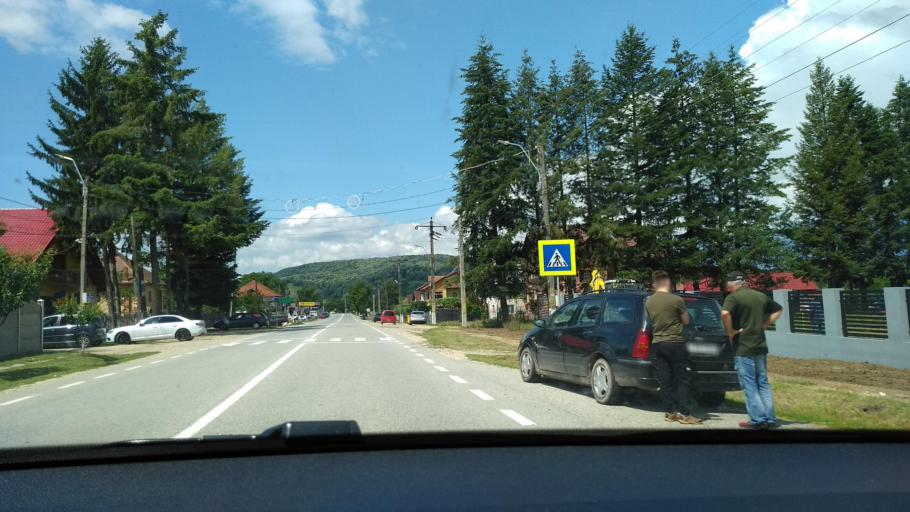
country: RO
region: Gorj
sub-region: Novaci
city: Pociovalistea
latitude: 45.1332
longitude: 23.6990
